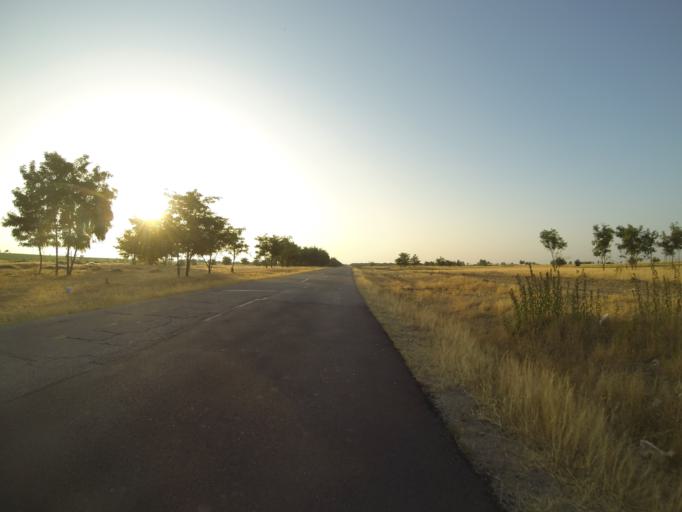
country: RO
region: Dolj
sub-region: Comuna Daneti
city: Daneti
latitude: 43.9720
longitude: 24.0686
